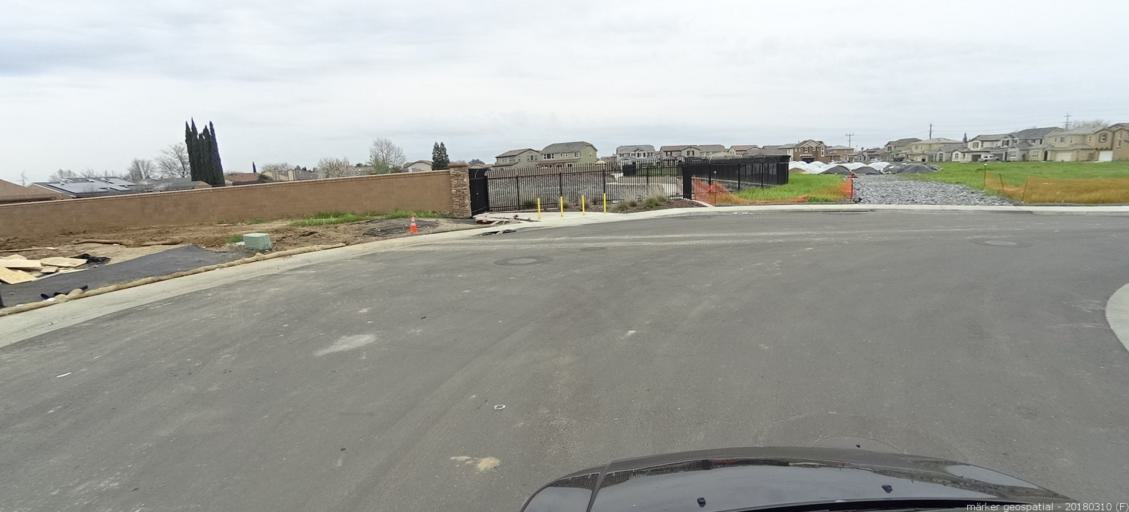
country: US
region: California
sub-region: Sacramento County
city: Vineyard
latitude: 38.4740
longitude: -121.3791
